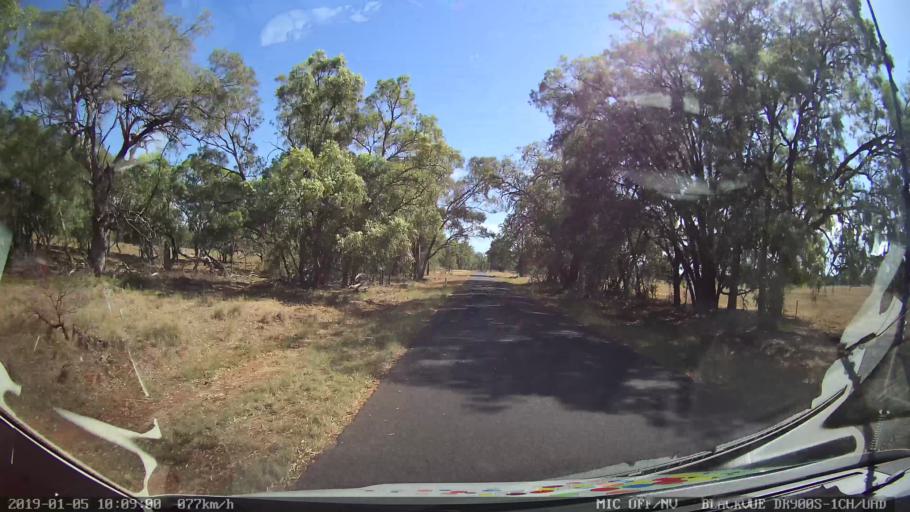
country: AU
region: New South Wales
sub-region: Gilgandra
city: Gilgandra
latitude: -31.6356
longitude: 148.8837
